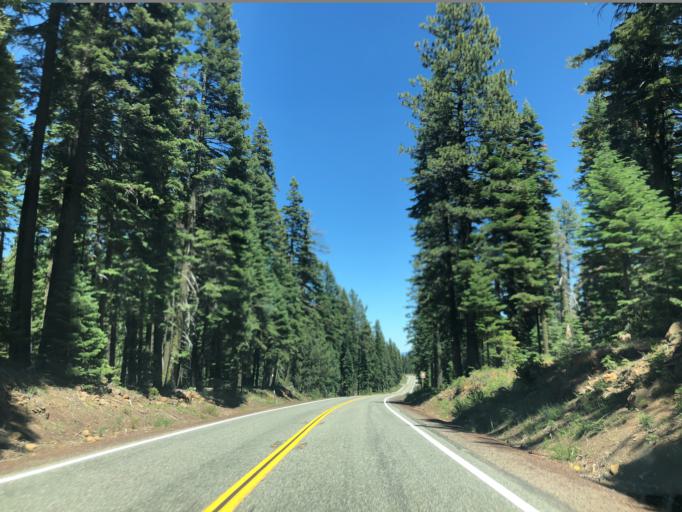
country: US
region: California
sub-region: Shasta County
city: Burney
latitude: 40.5882
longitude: -121.5472
